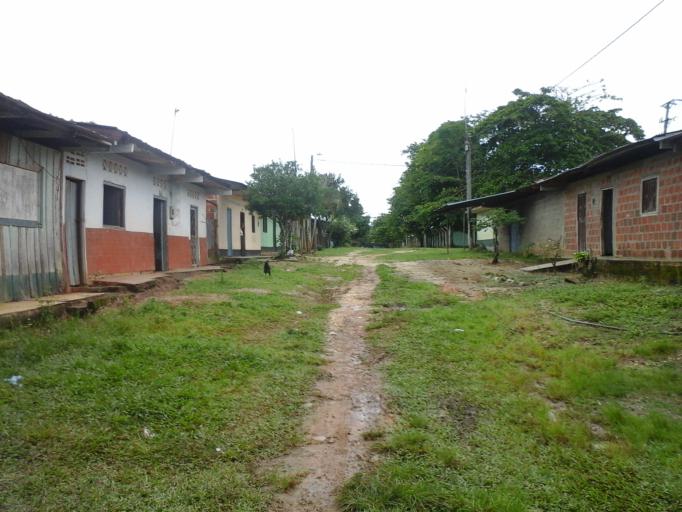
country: CO
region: Caqueta
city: El Doncello
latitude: 1.6134
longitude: -74.9979
